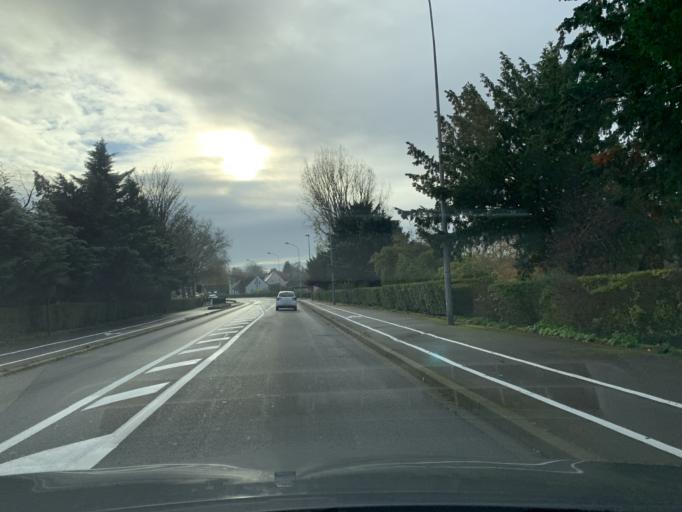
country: FR
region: Nord-Pas-de-Calais
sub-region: Departement du Nord
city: Lambres-lez-Douai
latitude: 50.3556
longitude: 3.0823
